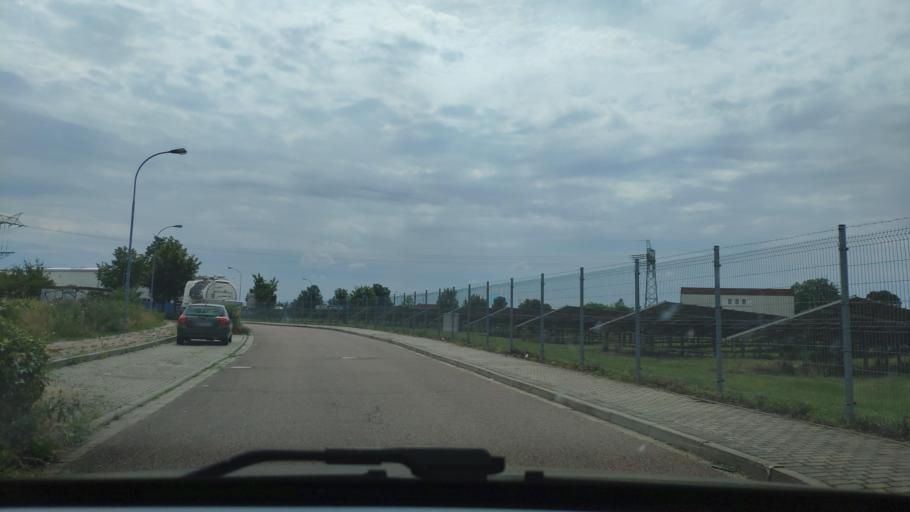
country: DE
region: Saxony-Anhalt
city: Bernburg
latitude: 51.7762
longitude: 11.7578
